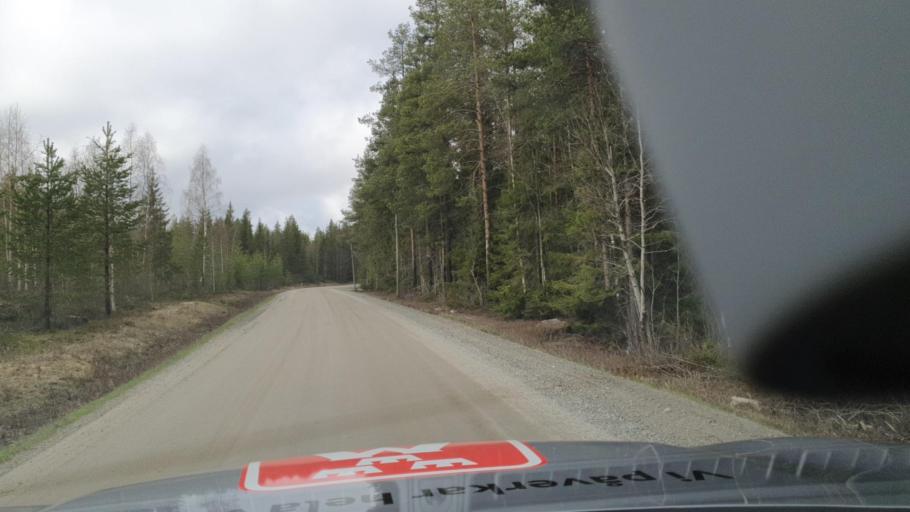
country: SE
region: Vaesterbotten
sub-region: Bjurholms Kommun
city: Bjurholm
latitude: 63.6837
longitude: 18.9781
